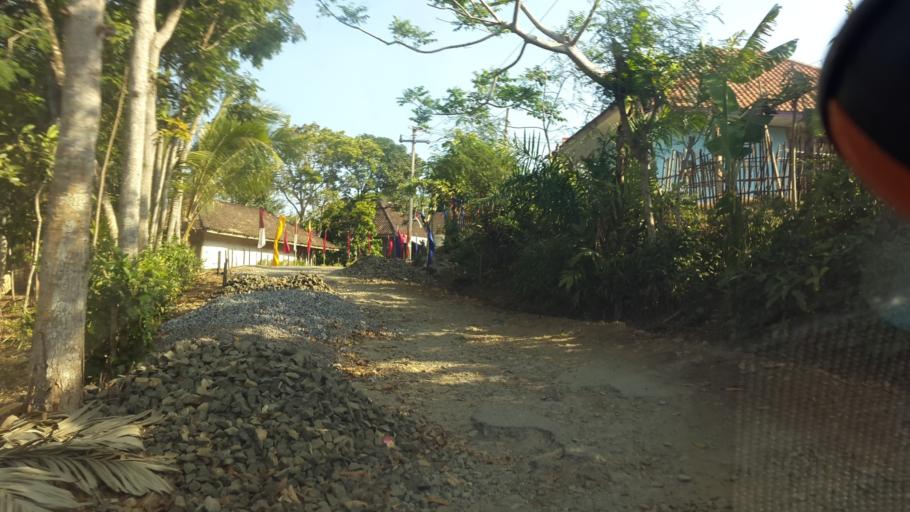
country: ID
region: West Java
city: Pasirpanjang
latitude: -7.2821
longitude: 106.4975
